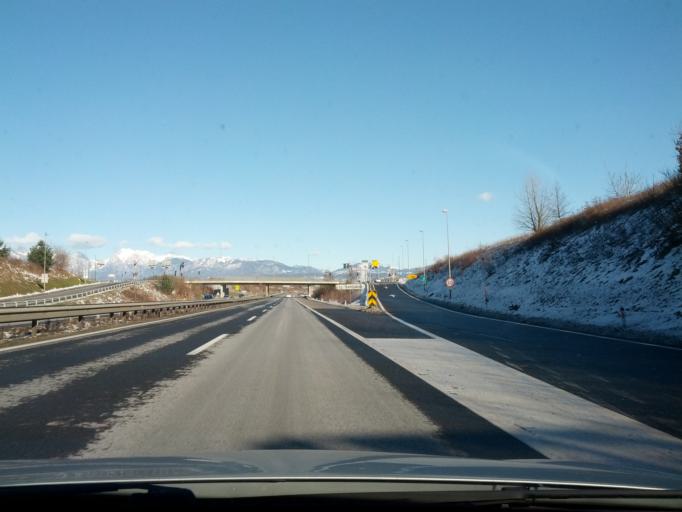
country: SI
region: Dol pri Ljubljani
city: Dol pri Ljubljani
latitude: 46.0890
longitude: 14.5860
